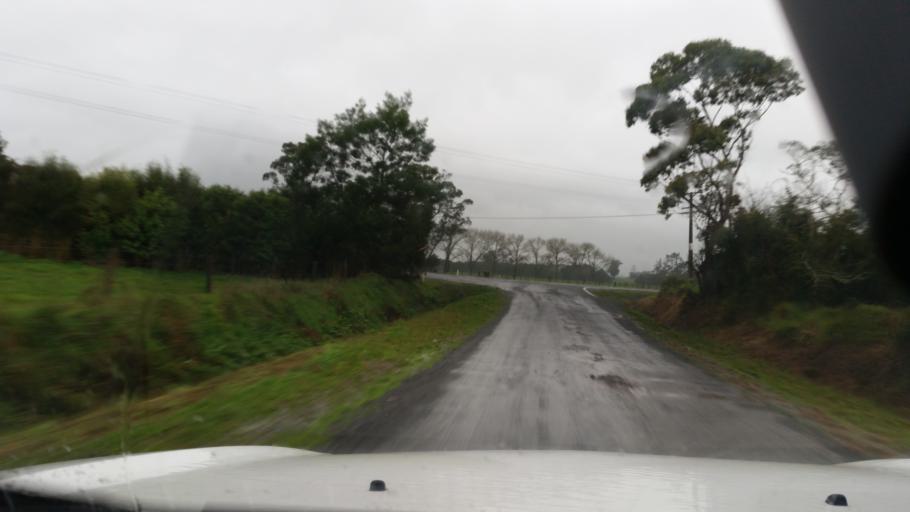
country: NZ
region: Northland
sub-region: Whangarei
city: Maungatapere
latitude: -35.7315
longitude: 174.0888
